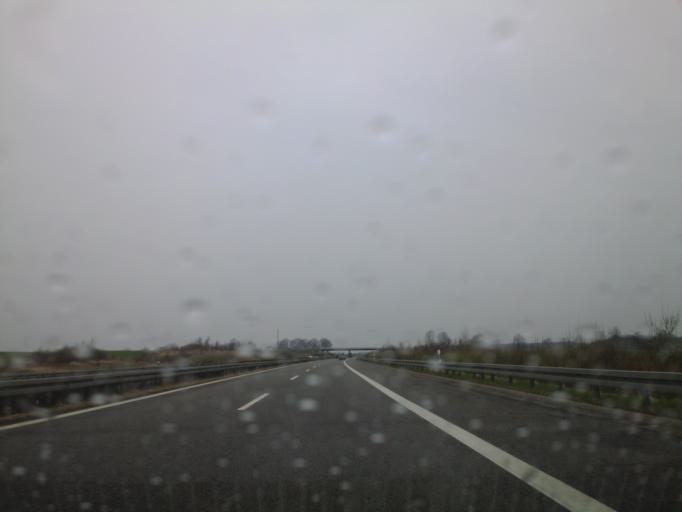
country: DE
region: Mecklenburg-Vorpommern
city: Tessin
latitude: 54.0154
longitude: 12.4417
